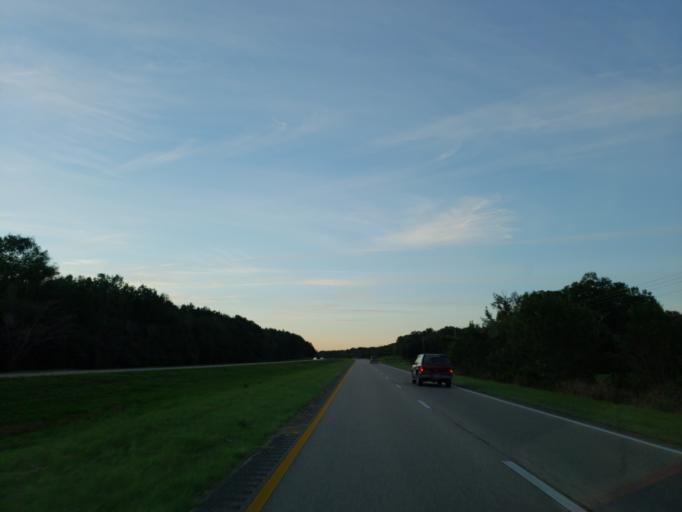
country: US
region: Mississippi
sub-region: Wayne County
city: Belmont
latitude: 31.5955
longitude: -88.5530
